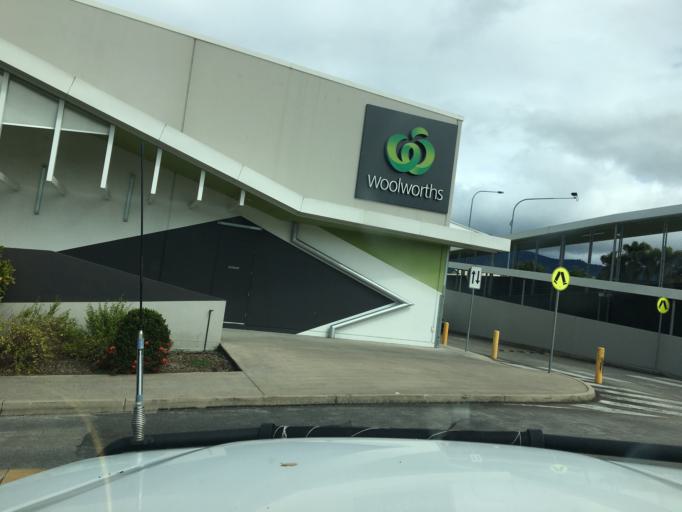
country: AU
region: Queensland
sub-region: Cairns
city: Woree
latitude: -16.9896
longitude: 145.7399
